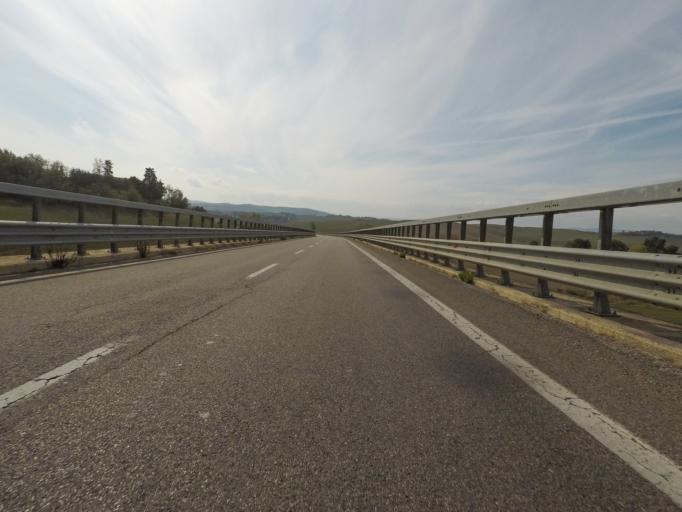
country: IT
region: Tuscany
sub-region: Provincia di Siena
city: Isola D'Arbia
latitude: 43.2687
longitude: 11.3301
